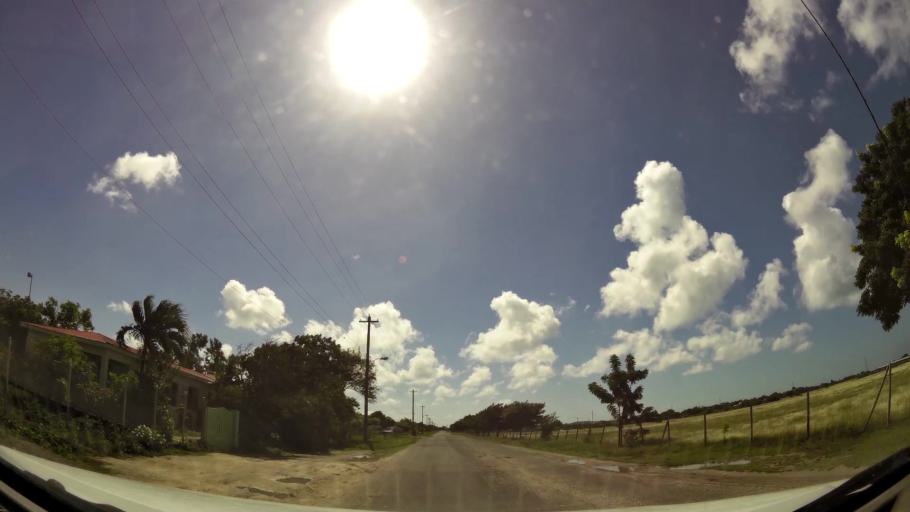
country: AG
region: Barbuda
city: Codrington
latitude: 17.6313
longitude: -61.8252
